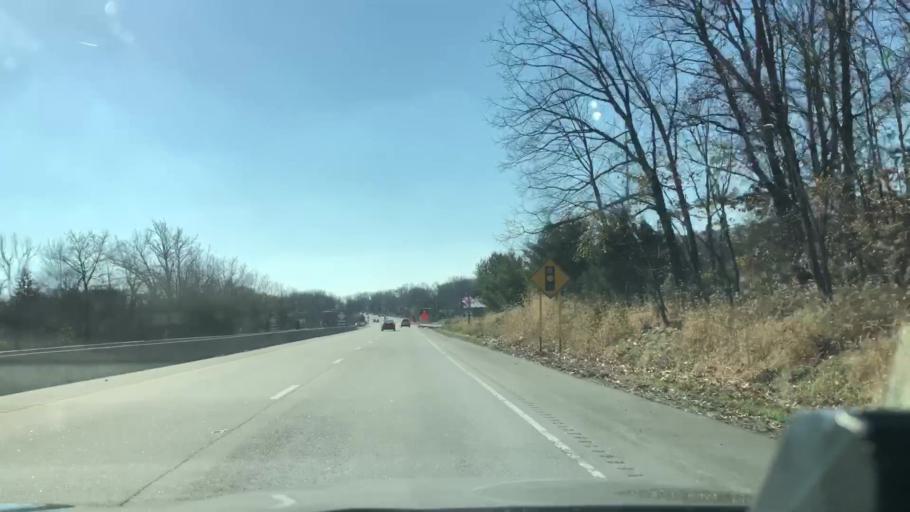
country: US
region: Pennsylvania
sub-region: Montgomery County
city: Halfway House
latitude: 40.2804
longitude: -75.6452
